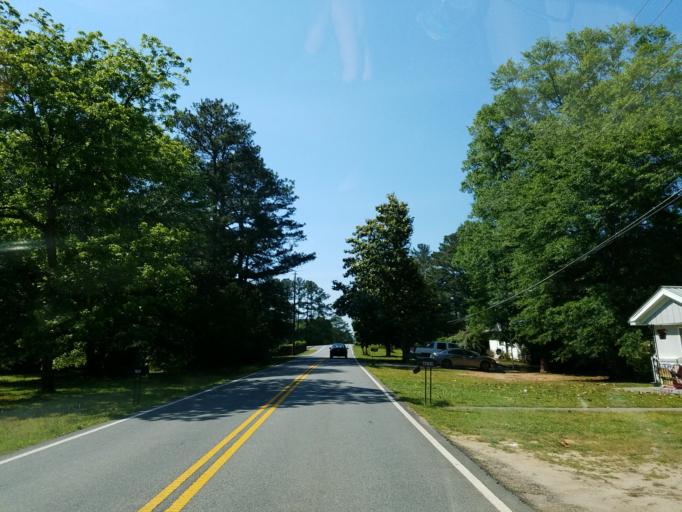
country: US
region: Georgia
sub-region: Cobb County
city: Marietta
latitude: 34.0048
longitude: -84.5077
